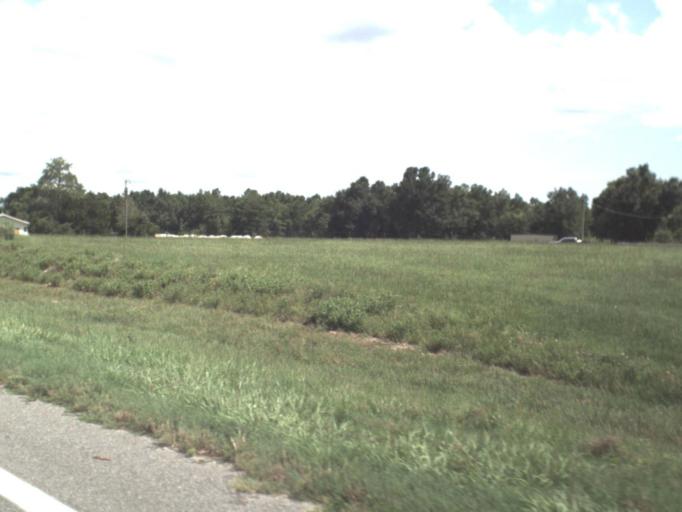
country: US
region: Florida
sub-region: Lafayette County
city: Mayo
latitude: 29.9535
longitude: -82.9591
